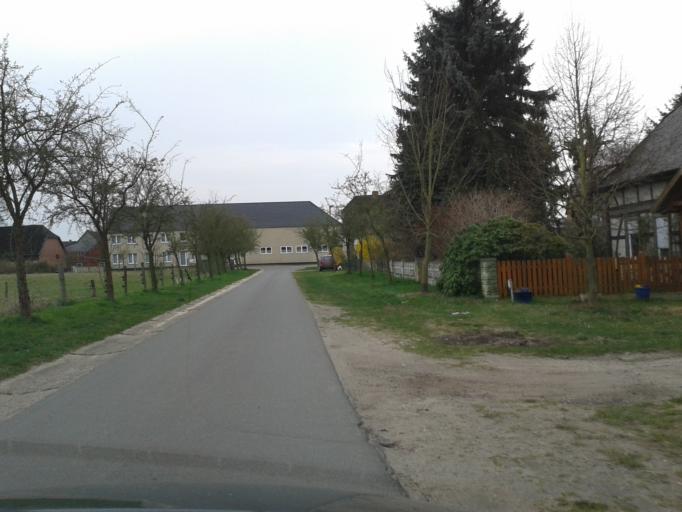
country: DE
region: Lower Saxony
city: Woltersdorf
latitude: 52.9200
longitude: 11.2227
